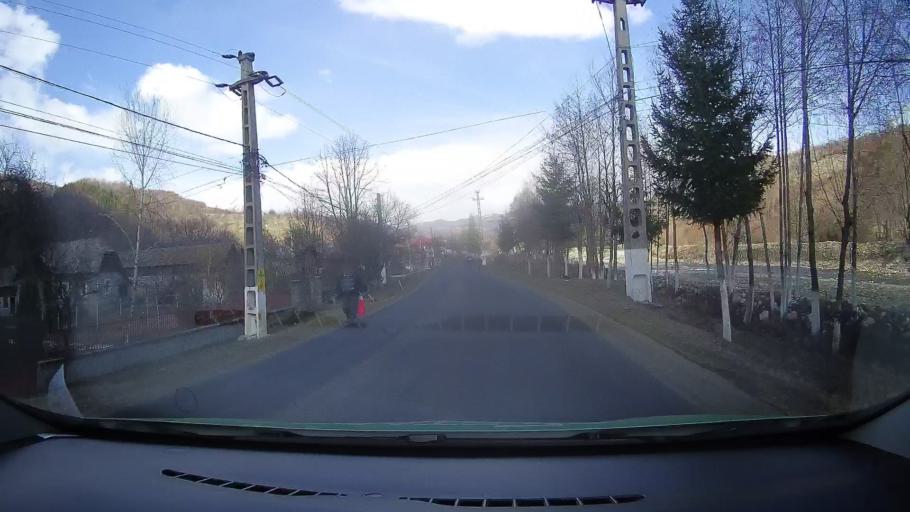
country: RO
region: Dambovita
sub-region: Comuna Runcu
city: Badeni
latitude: 45.1600
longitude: 25.3971
